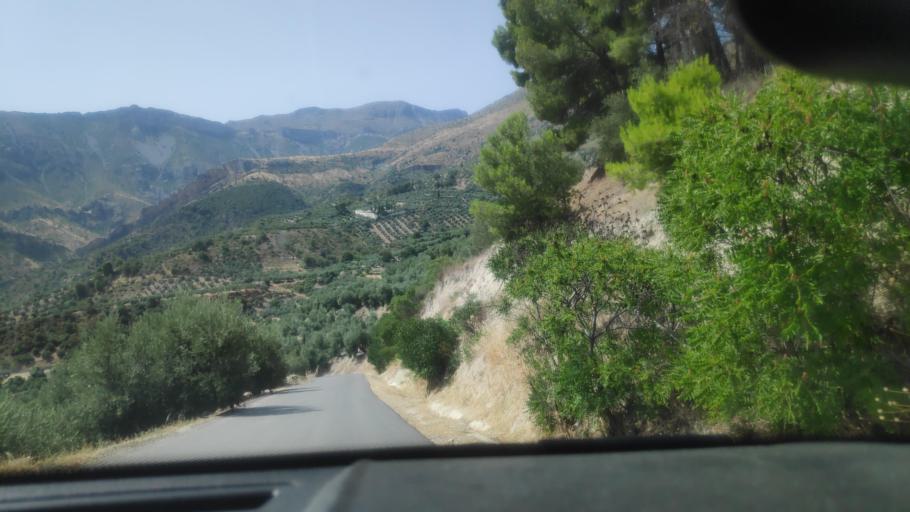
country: ES
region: Andalusia
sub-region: Provincia de Jaen
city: Torres
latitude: 37.7915
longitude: -3.4620
